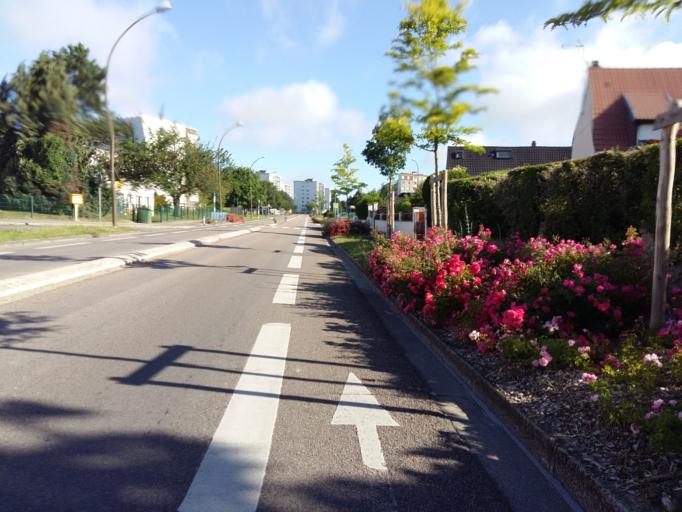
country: FR
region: Picardie
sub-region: Departement de la Somme
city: Rivery
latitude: 49.9106
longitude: 2.3252
